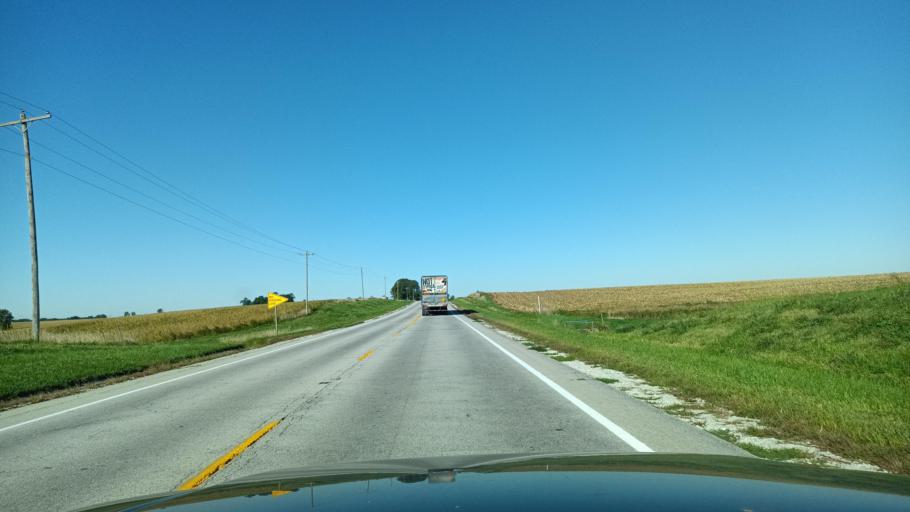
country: US
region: Illinois
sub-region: Warren County
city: Monmouth
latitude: 40.8500
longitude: -90.7712
